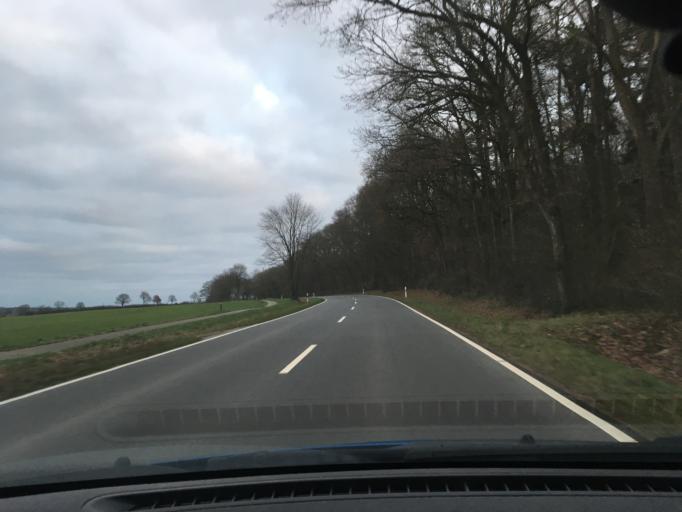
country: DE
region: Schleswig-Holstein
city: Mehlbek
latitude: 53.9965
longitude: 9.4459
